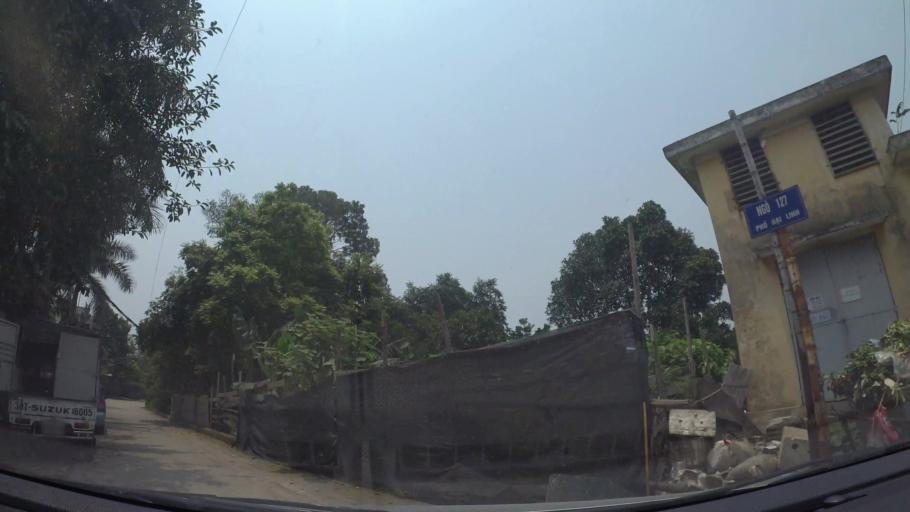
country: VN
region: Ha Noi
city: Ha Dong
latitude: 20.9954
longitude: 105.7719
